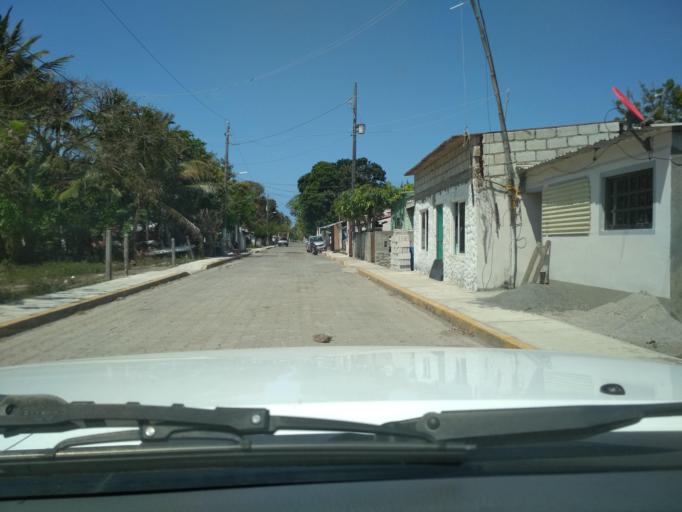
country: MX
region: Veracruz
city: Anton Lizardo
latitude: 19.0116
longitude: -95.9674
